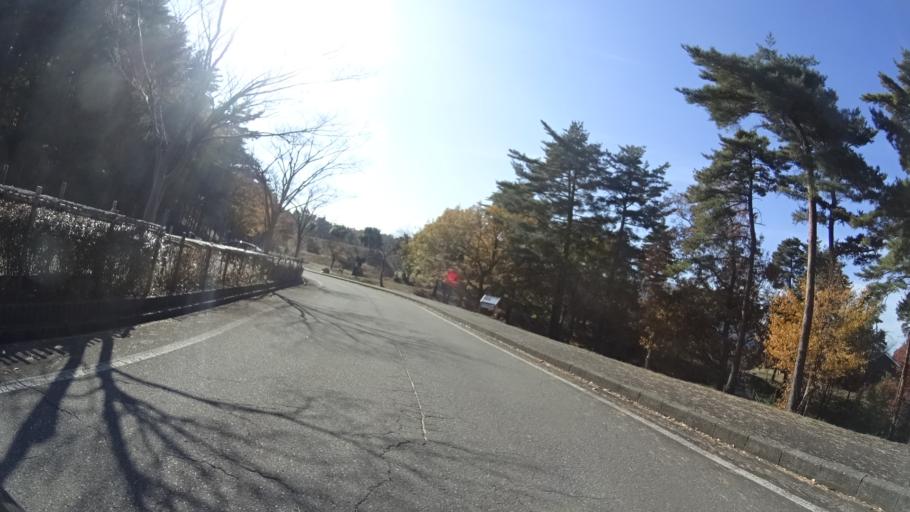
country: JP
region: Niigata
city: Itoigawa
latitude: 37.0250
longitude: 137.8690
